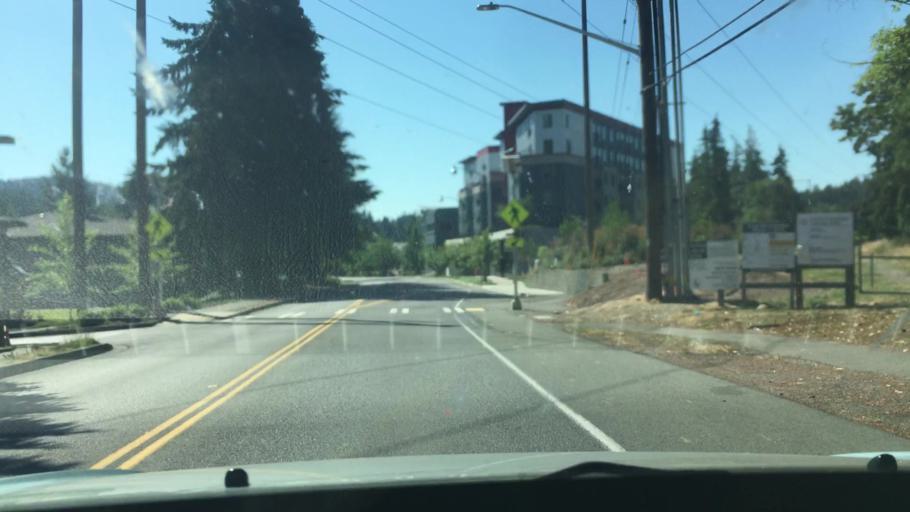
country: US
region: Washington
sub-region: King County
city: Newcastle
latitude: 47.5401
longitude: -122.1698
